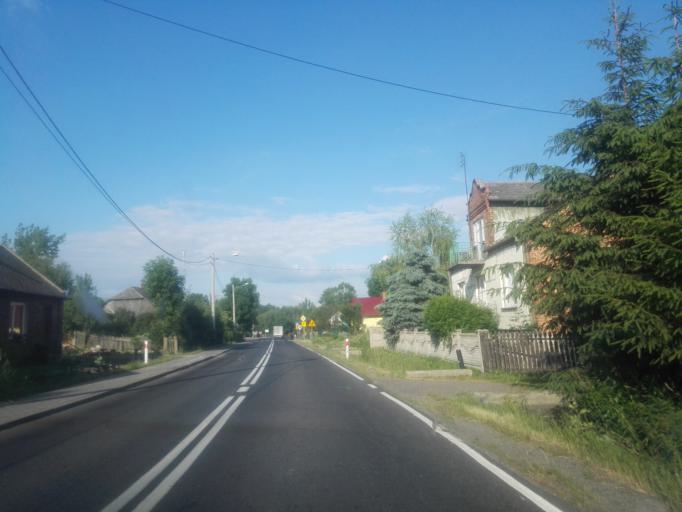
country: PL
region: Silesian Voivodeship
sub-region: Powiat czestochowski
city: Lelow
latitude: 50.6549
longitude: 19.7231
